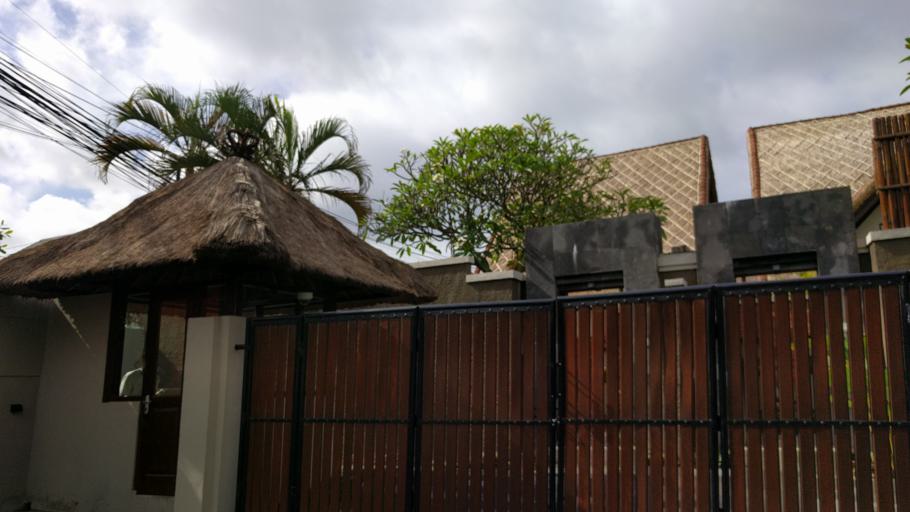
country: ID
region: Bali
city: Kuta
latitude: -8.6824
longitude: 115.1599
